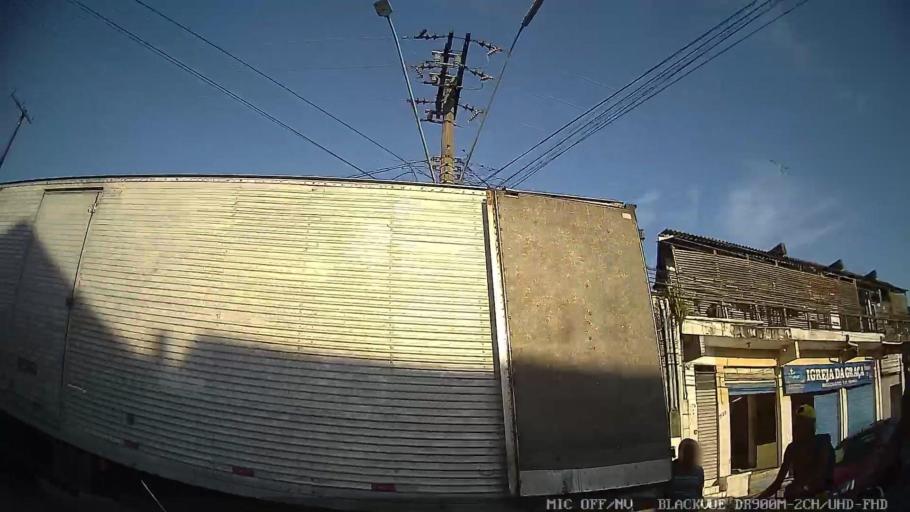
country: BR
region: Sao Paulo
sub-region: Guaruja
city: Guaruja
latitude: -23.9770
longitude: -46.2595
